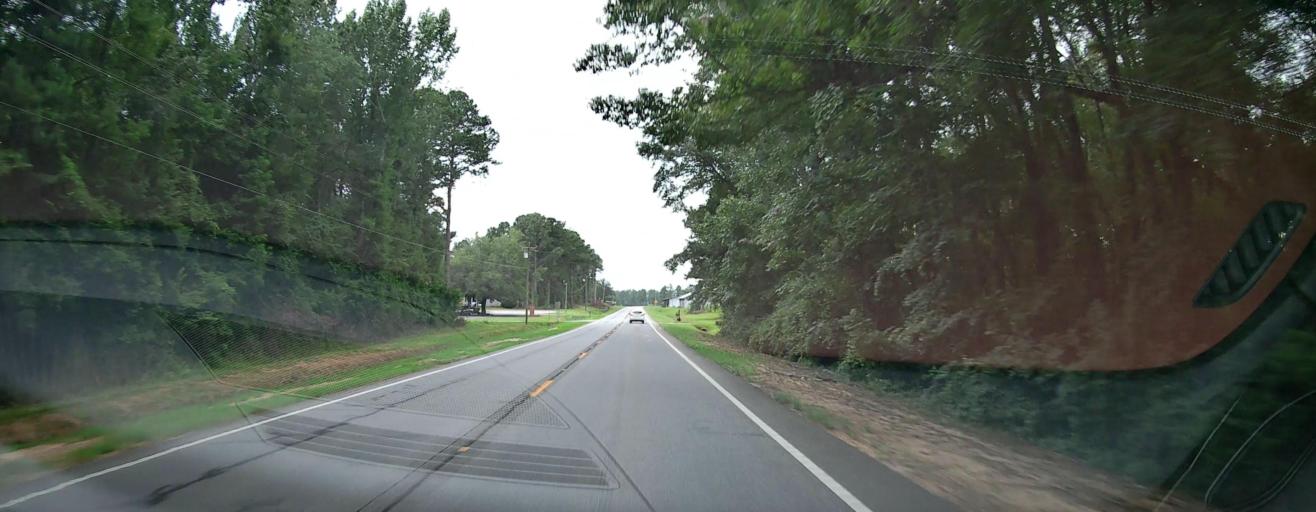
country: US
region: Georgia
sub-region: Laurens County
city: East Dublin
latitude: 32.5834
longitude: -82.8351
